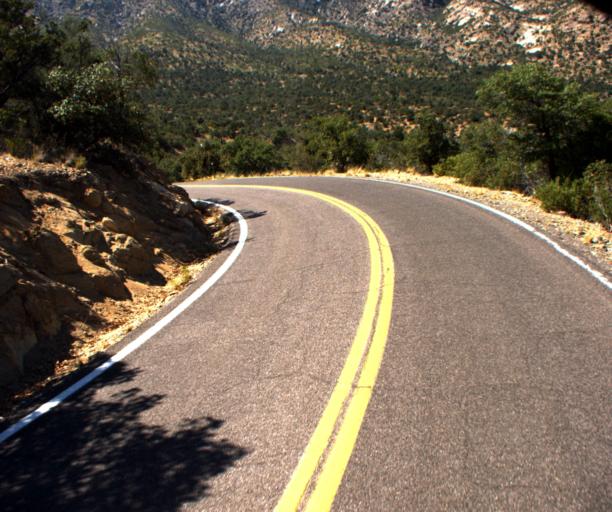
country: US
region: Arizona
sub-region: Graham County
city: Swift Trail Junction
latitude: 32.6638
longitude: -109.8004
